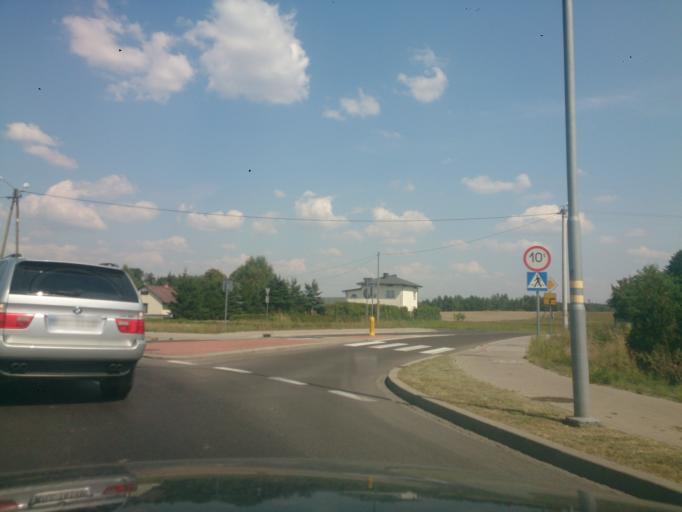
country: PL
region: Subcarpathian Voivodeship
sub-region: Powiat kolbuszowski
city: Kolbuszowa
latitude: 50.2512
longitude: 21.7736
